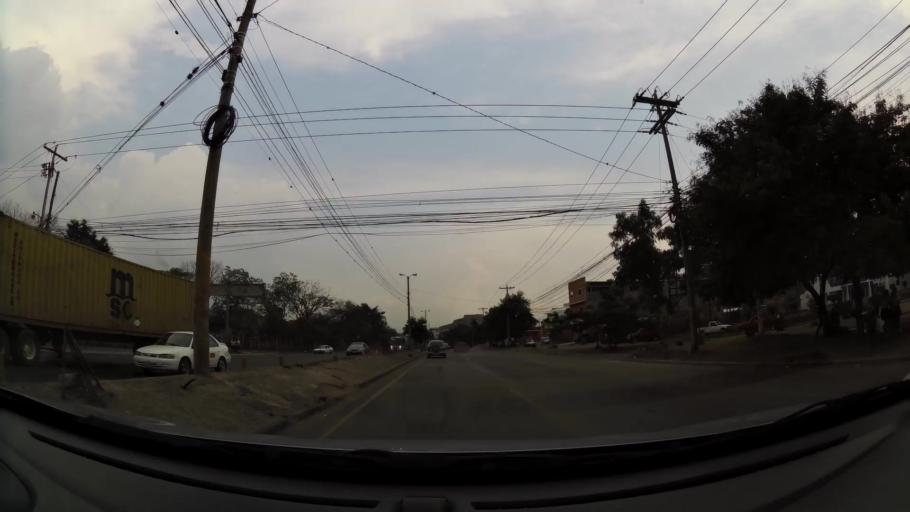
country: HN
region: Francisco Morazan
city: Tegucigalpa
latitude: 14.0798
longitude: -87.2169
